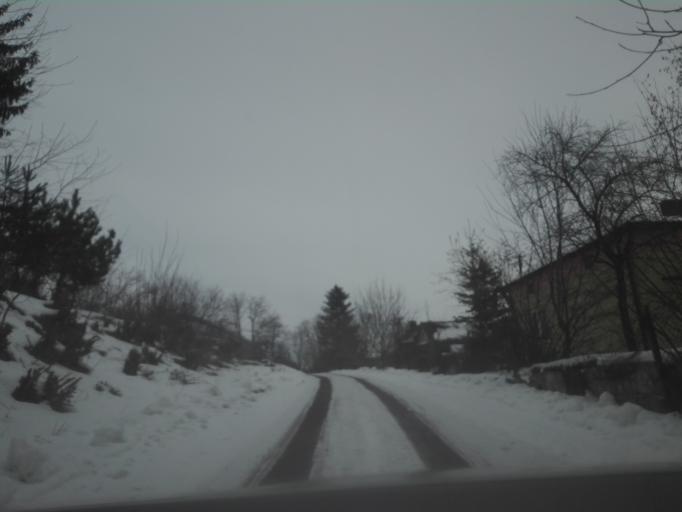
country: PL
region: Lublin Voivodeship
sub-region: Powiat hrubieszowski
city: Horodlo
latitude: 50.8478
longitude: 24.0284
